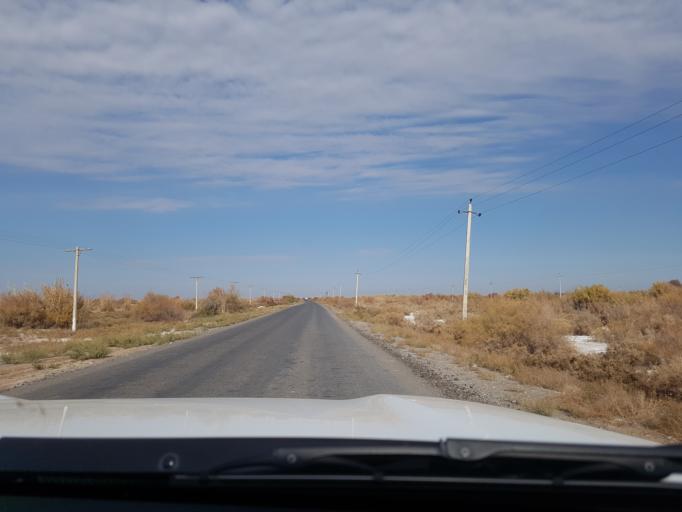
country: TM
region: Ahal
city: Tejen
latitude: 37.3610
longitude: 61.0927
